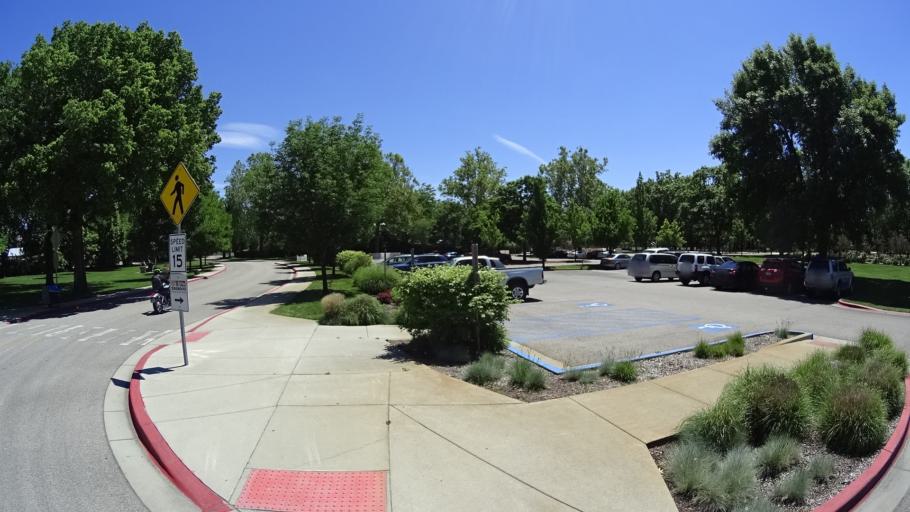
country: US
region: Idaho
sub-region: Ada County
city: Boise
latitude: 43.6097
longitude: -116.2043
